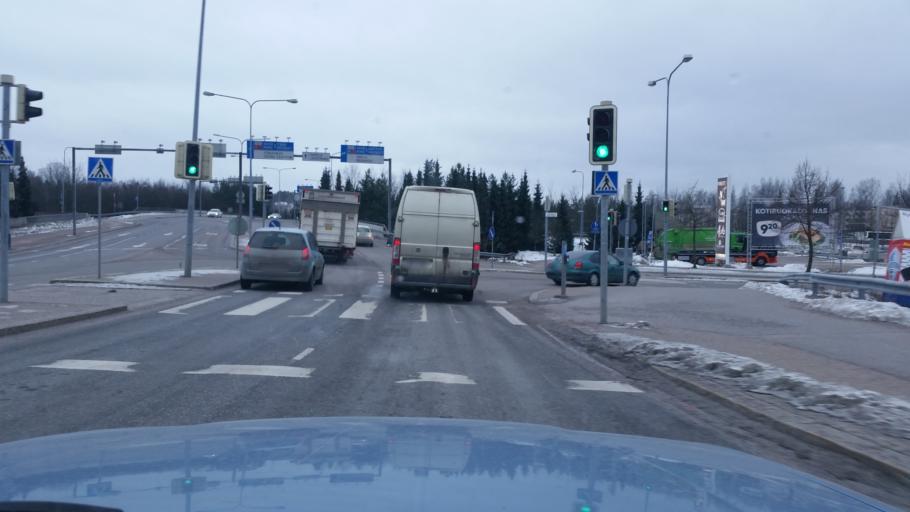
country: FI
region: Uusimaa
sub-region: Helsinki
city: Vantaa
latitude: 60.2431
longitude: 24.9965
